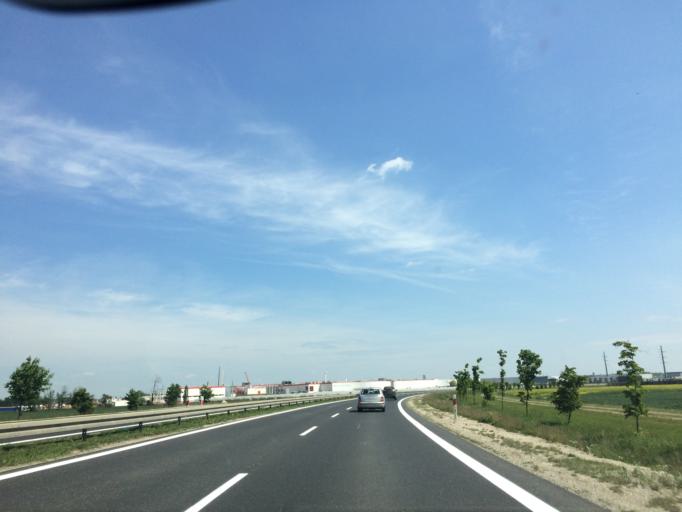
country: PL
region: Lower Silesian Voivodeship
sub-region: Powiat wroclawski
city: Tyniec Maly
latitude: 51.0308
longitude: 16.9129
